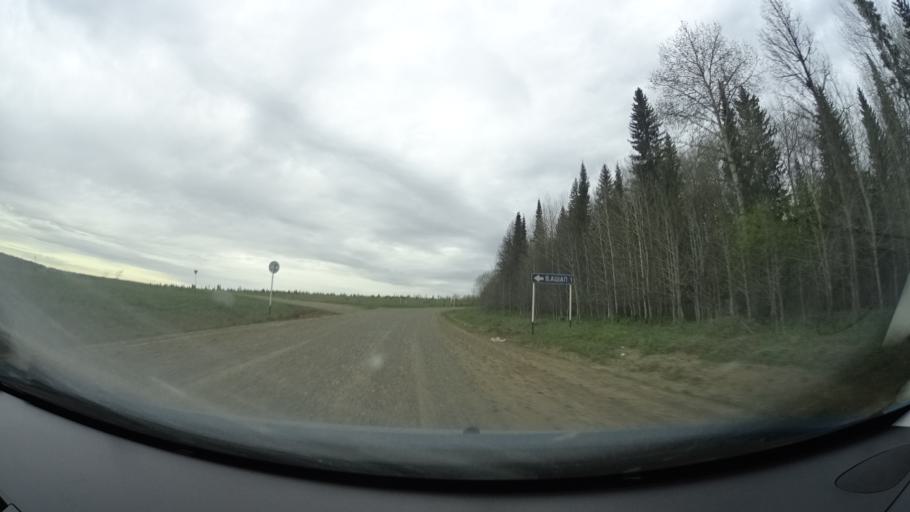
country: RU
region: Perm
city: Kuyeda
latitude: 56.6055
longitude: 55.7134
